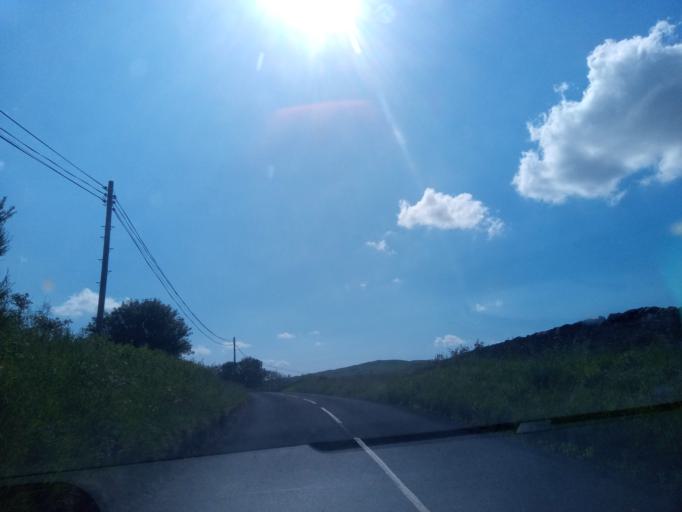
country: GB
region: Scotland
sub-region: The Scottish Borders
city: Innerleithen
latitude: 55.5382
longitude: -3.0250
